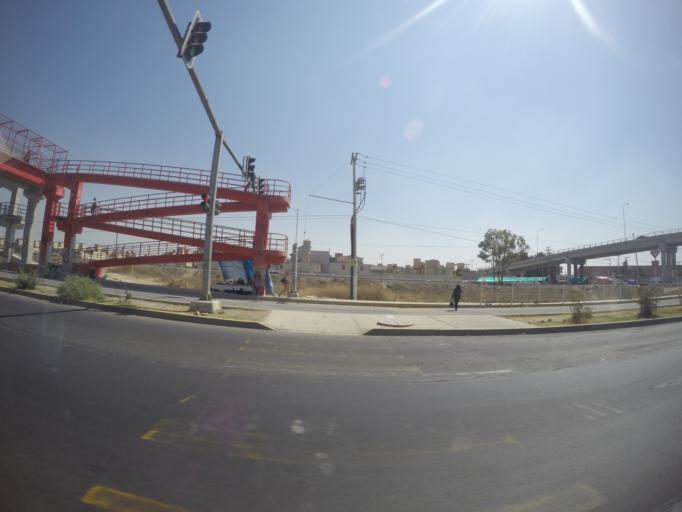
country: MX
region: Mexico
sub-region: Atenco
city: Colonia el Salado
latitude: 19.5882
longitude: -99.0240
